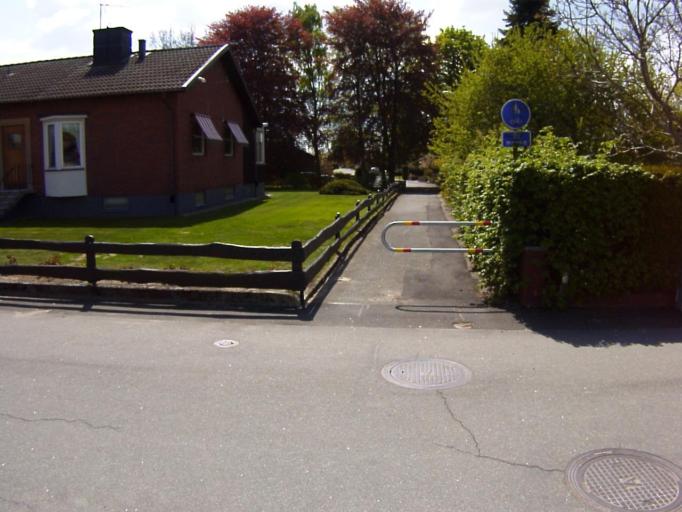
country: SE
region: Skane
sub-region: Kristianstads Kommun
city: Fjalkinge
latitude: 56.0159
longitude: 14.2273
